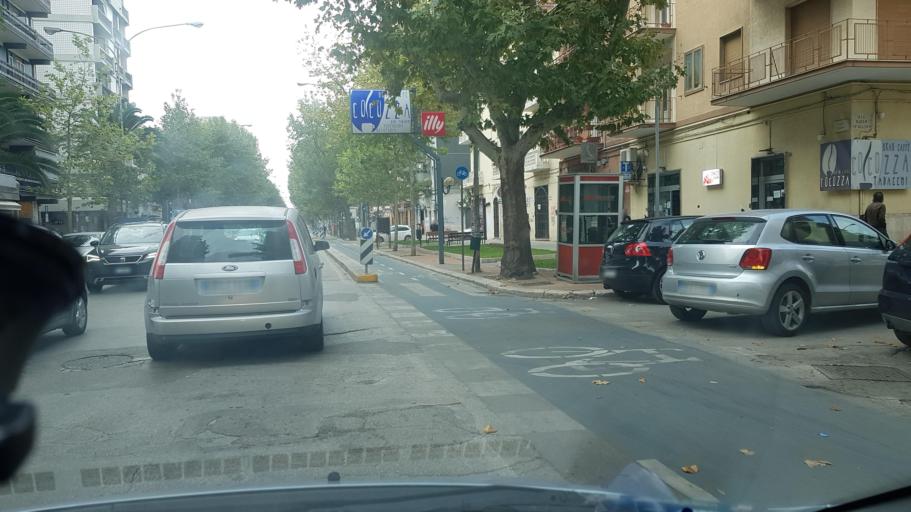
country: IT
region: Apulia
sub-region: Provincia di Foggia
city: Foggia
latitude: 41.4589
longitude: 15.5528
